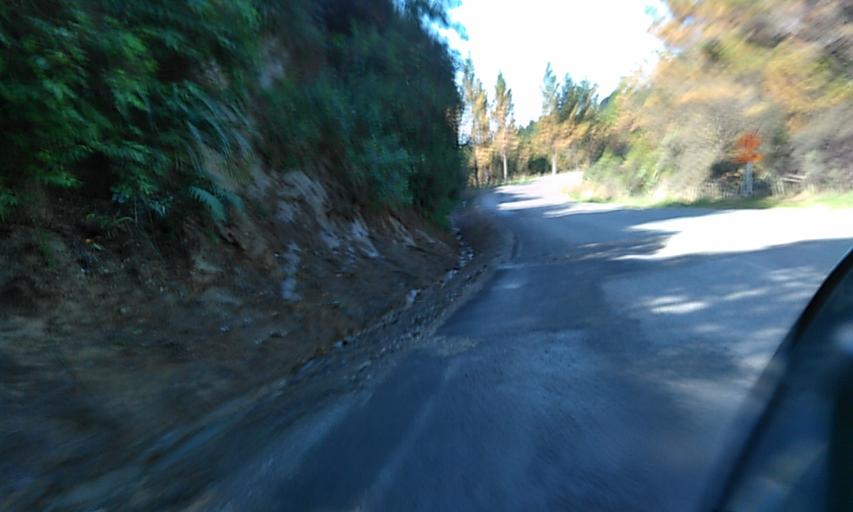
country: NZ
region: Gisborne
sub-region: Gisborne District
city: Gisborne
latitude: -38.2977
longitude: 178.1019
